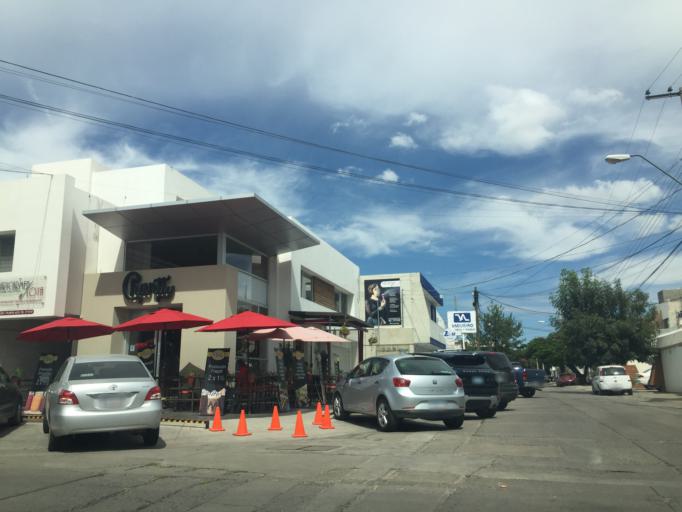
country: MX
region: Guanajuato
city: Leon
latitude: 21.1545
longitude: -101.6927
